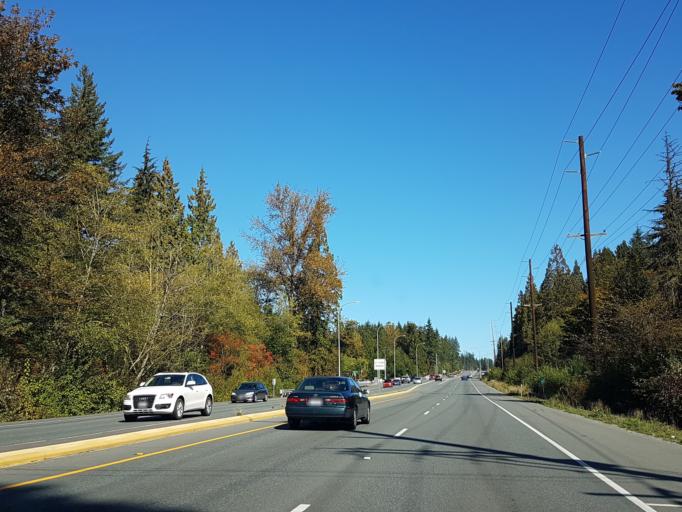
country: US
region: Washington
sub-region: Snohomish County
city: Clearview
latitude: 47.8104
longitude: -122.1419
